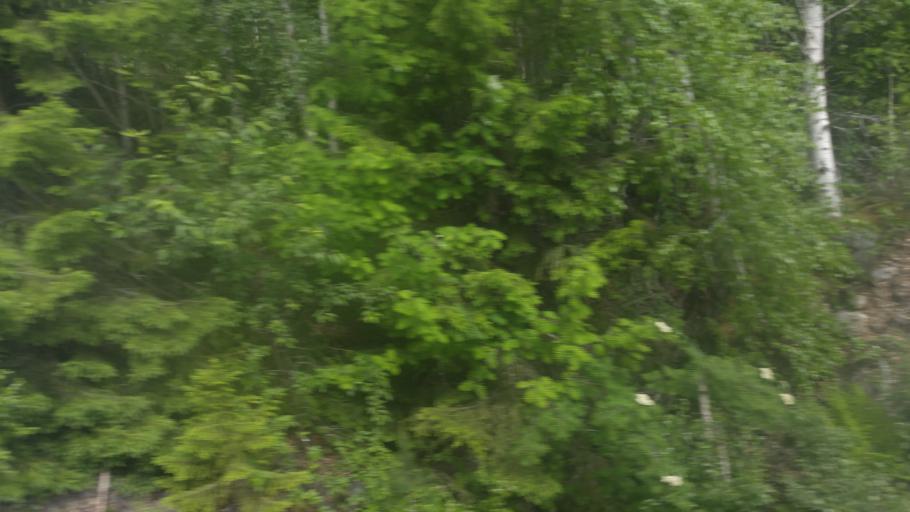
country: NO
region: Sor-Trondelag
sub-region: Selbu
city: Mebonden
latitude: 62.9577
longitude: 10.8031
